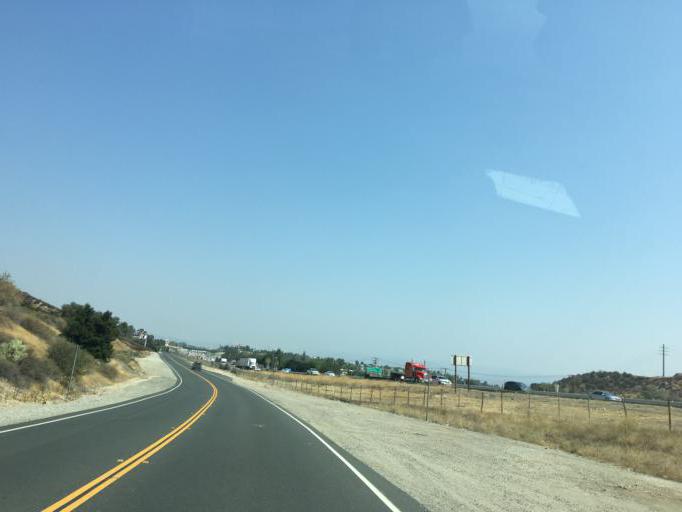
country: US
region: California
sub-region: Los Angeles County
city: Santa Clarita
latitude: 34.3655
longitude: -118.5575
